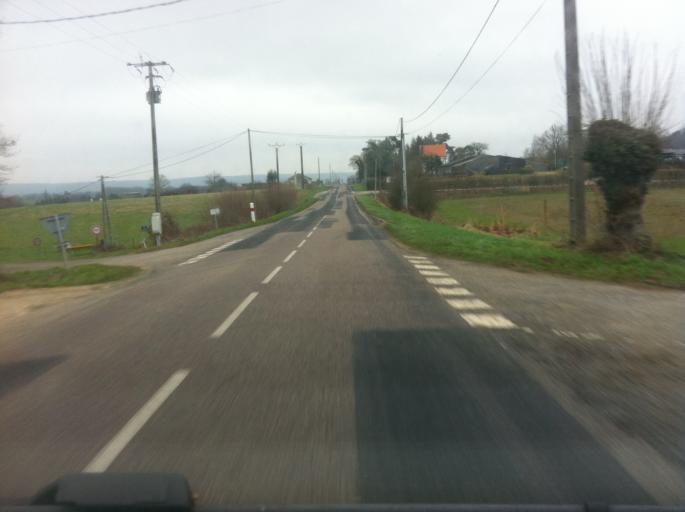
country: FR
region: Haute-Normandie
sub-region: Departement de la Seine-Maritime
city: La Mailleraye-sur-Seine
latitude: 49.4705
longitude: 0.7418
